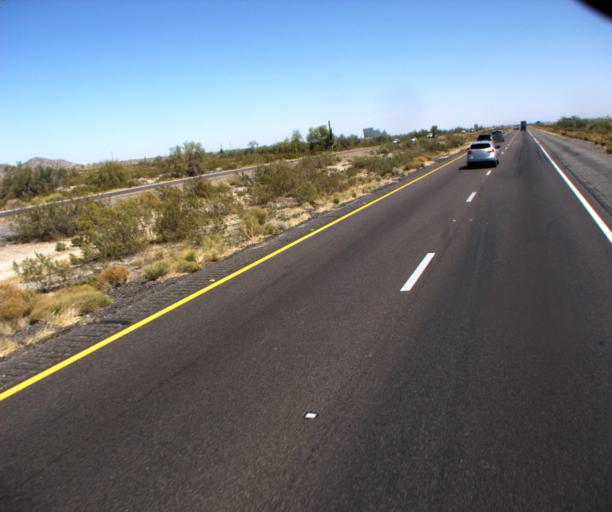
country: US
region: Arizona
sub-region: Maricopa County
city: Buckeye
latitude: 33.4512
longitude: -112.5359
